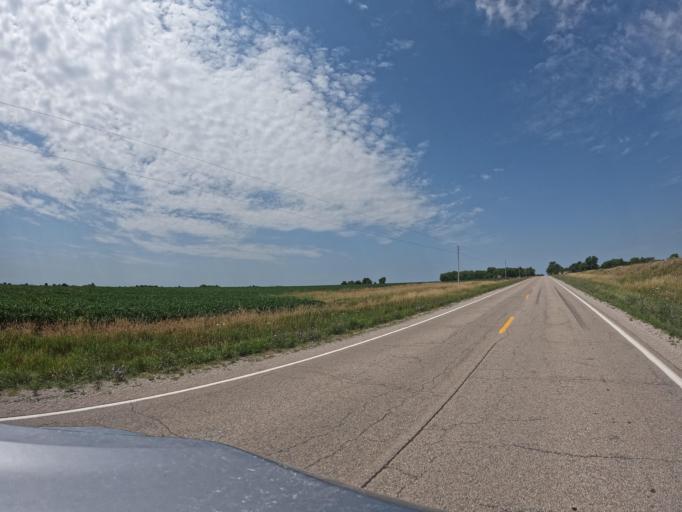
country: US
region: Iowa
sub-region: Appanoose County
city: Centerville
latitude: 40.8123
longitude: -92.9387
